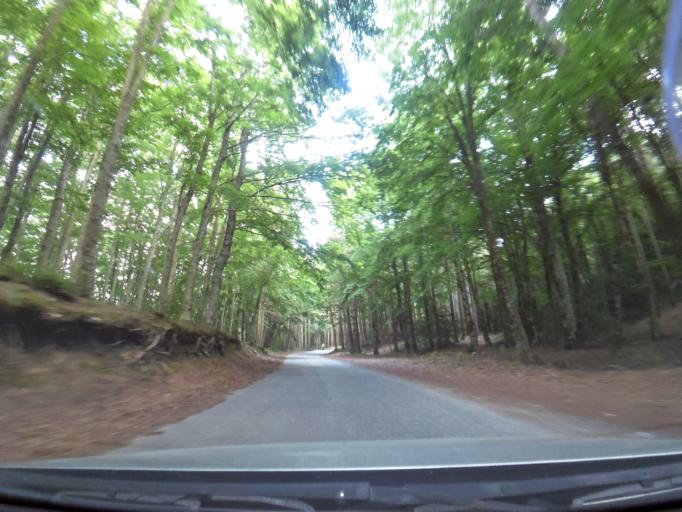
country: IT
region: Calabria
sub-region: Provincia di Vibo-Valentia
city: Nardodipace
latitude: 38.5036
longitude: 16.3801
